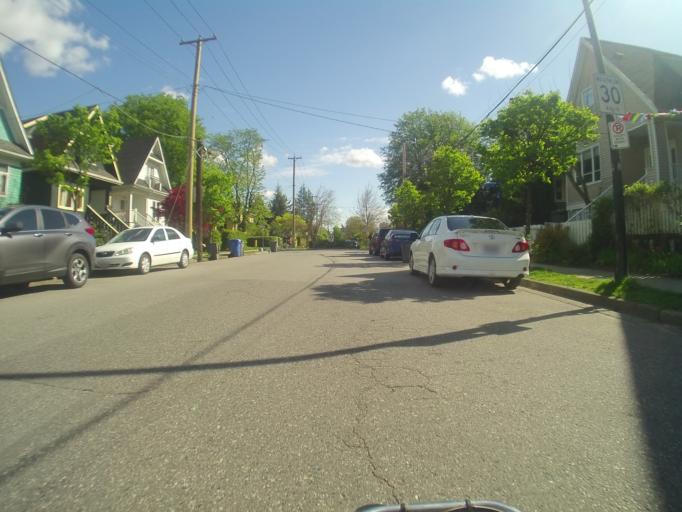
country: CA
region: British Columbia
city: Vancouver
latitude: 49.2618
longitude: -123.0737
